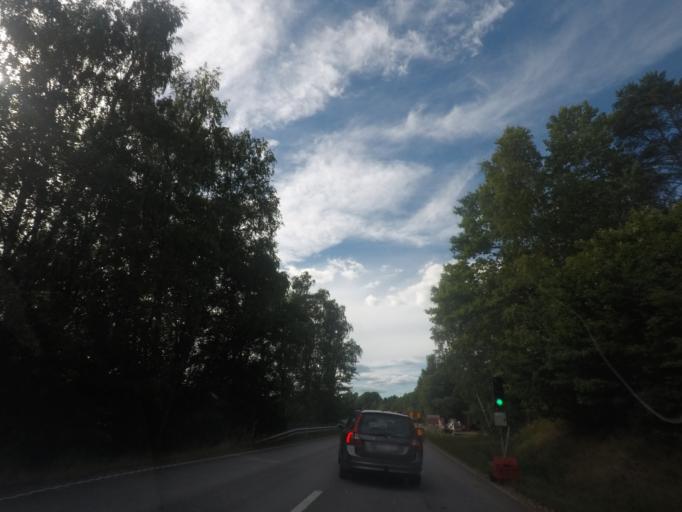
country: SE
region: Stockholm
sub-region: Norrtalje Kommun
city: Skanninge
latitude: 59.9024
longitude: 18.5918
